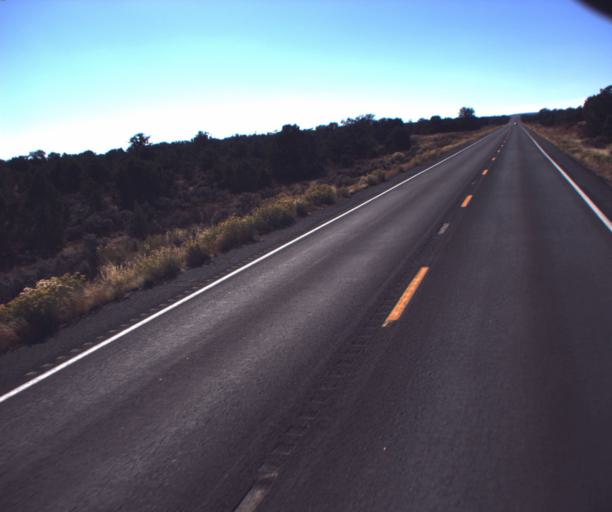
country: US
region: Arizona
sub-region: Coconino County
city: Kaibito
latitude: 36.5830
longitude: -110.8366
